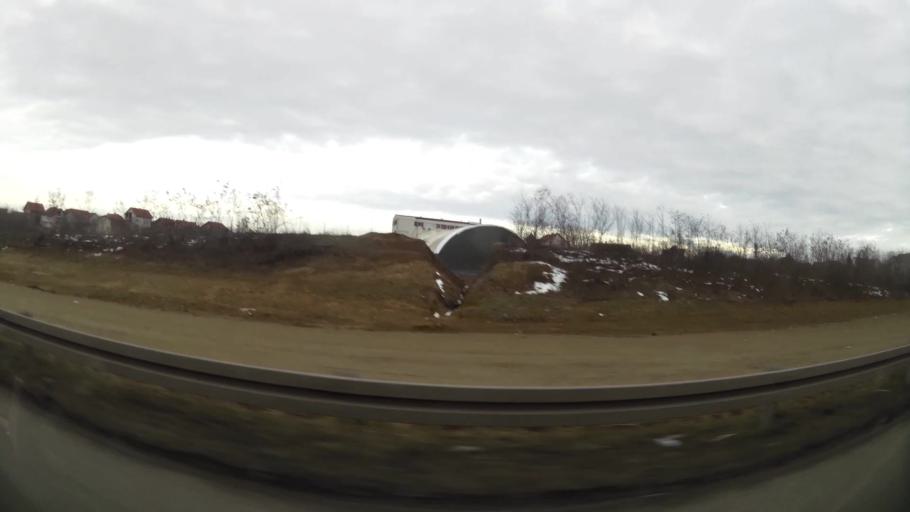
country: RS
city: Ostruznica
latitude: 44.7157
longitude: 20.3616
